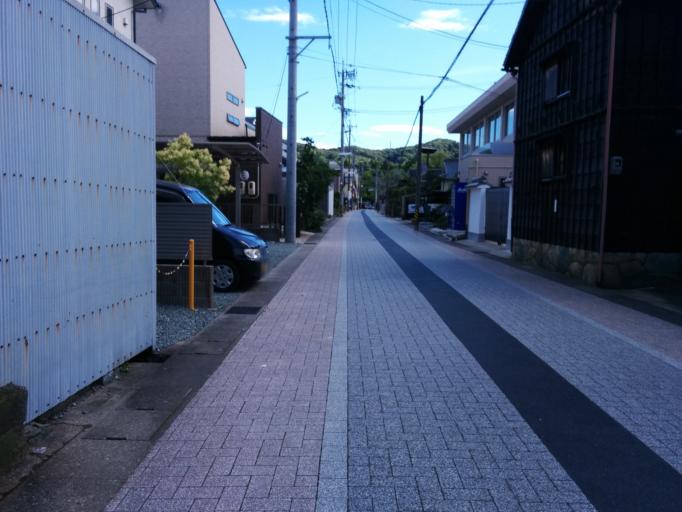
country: JP
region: Mie
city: Ise
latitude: 34.4913
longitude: 136.7052
